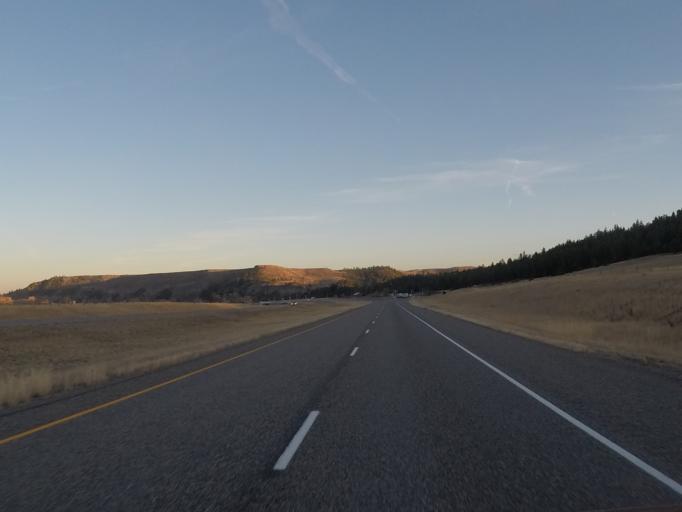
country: US
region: Montana
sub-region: Sweet Grass County
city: Big Timber
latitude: 45.7388
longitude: -109.7630
